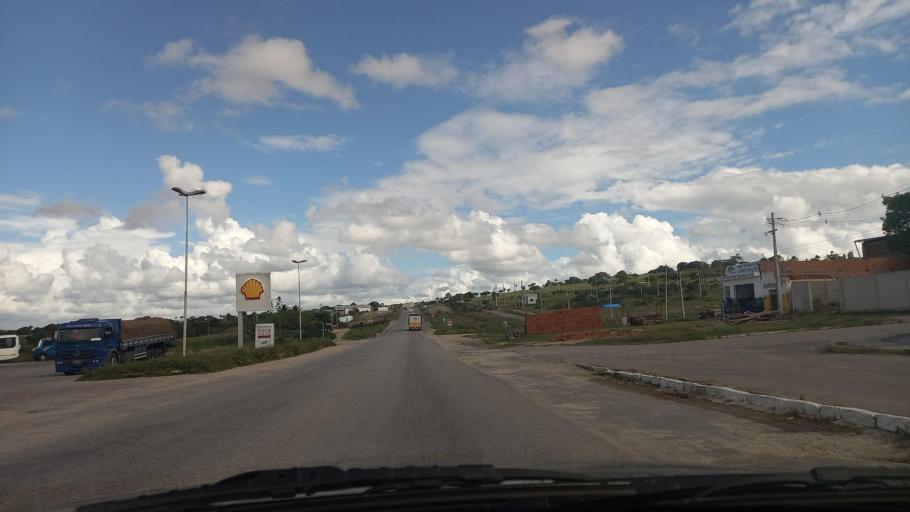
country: BR
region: Pernambuco
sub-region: Sao Joao
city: Sao Joao
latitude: -8.7557
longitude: -36.4307
